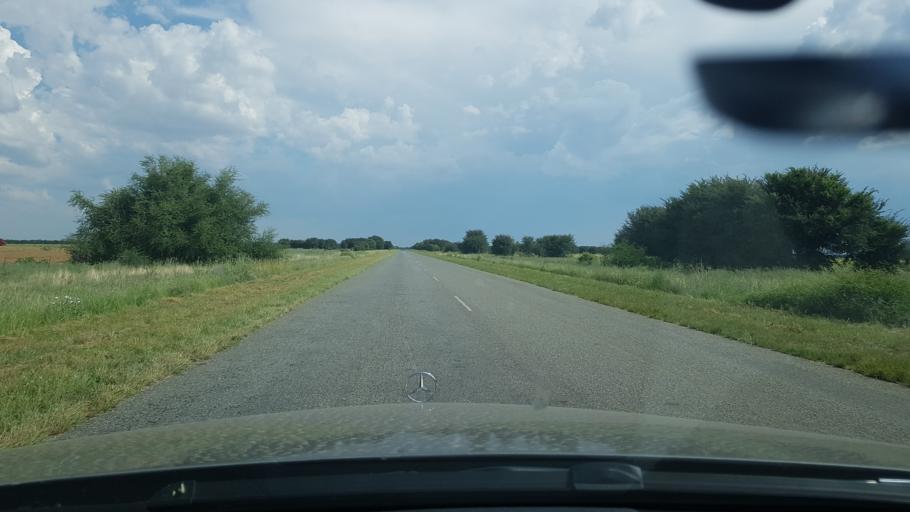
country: ZA
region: North-West
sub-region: Dr Ruth Segomotsi Mompati District Municipality
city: Bloemhof
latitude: -27.7022
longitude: 25.5831
